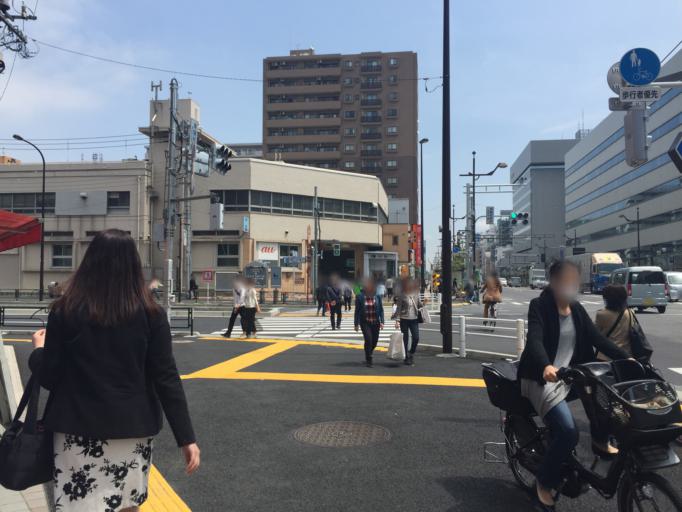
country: JP
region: Tokyo
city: Urayasu
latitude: 35.6696
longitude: 139.8162
